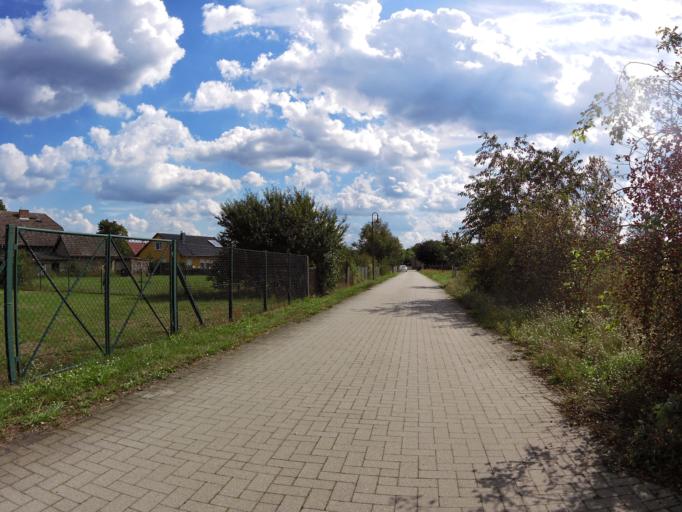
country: DE
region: Brandenburg
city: Storkow
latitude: 52.2186
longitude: 13.8731
